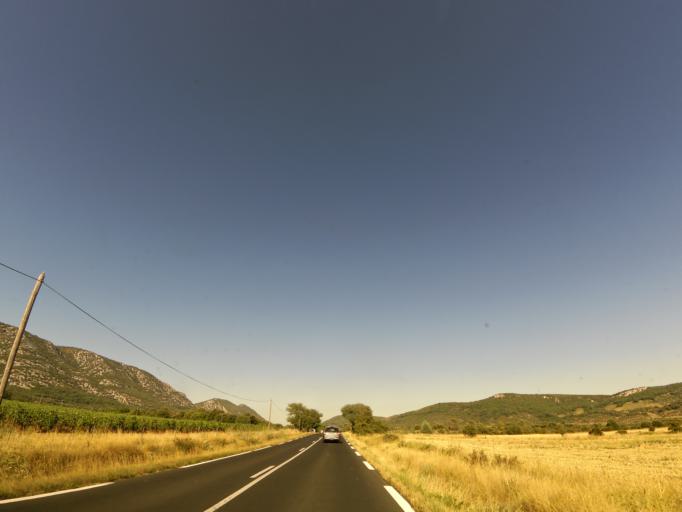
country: FR
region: Languedoc-Roussillon
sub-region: Departement de l'Herault
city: Laroque
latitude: 43.9486
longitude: 3.7735
